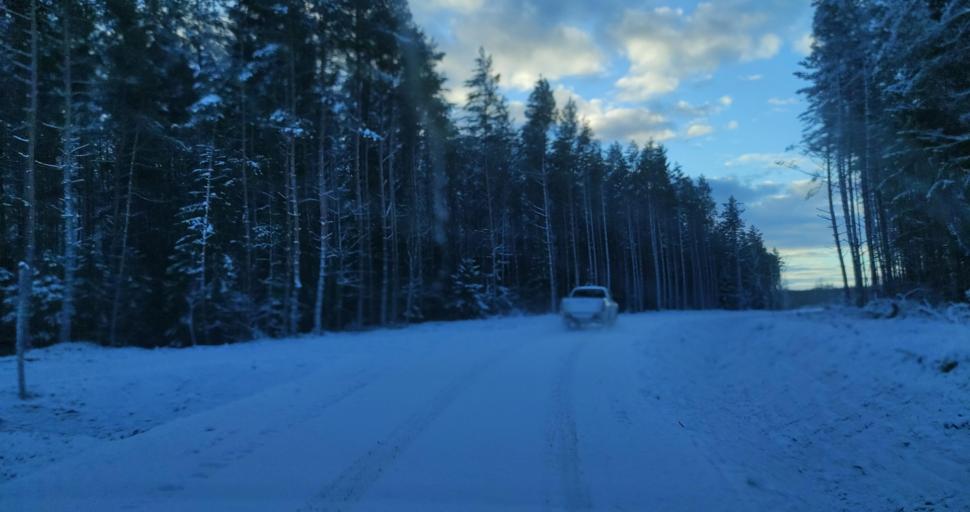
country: LV
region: Skrunda
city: Skrunda
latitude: 56.5902
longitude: 21.9525
